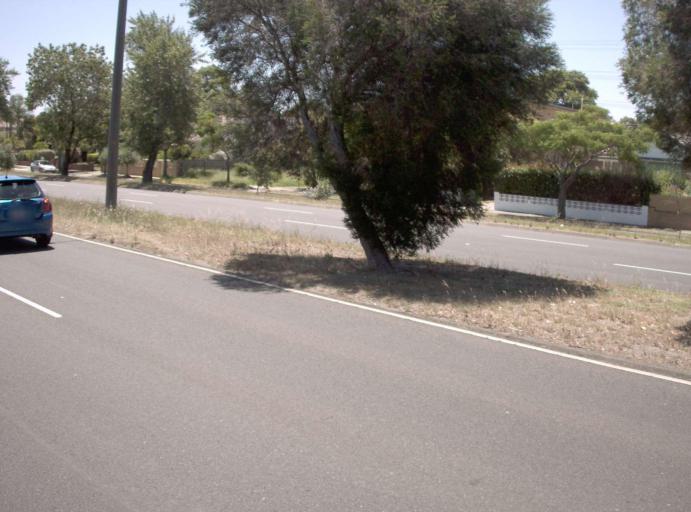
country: AU
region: Victoria
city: Clayton
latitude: -37.9023
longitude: 145.1076
